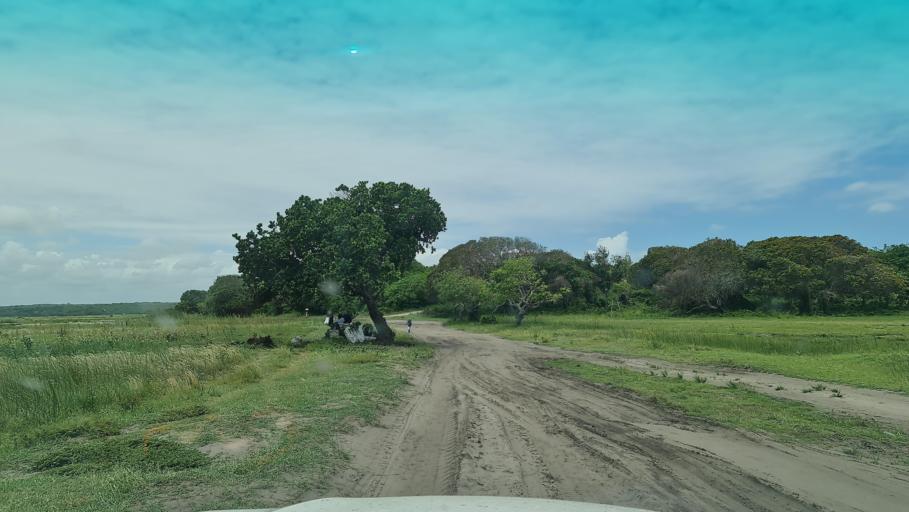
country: MZ
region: Maputo
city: Manhica
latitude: -25.5241
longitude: 32.8597
